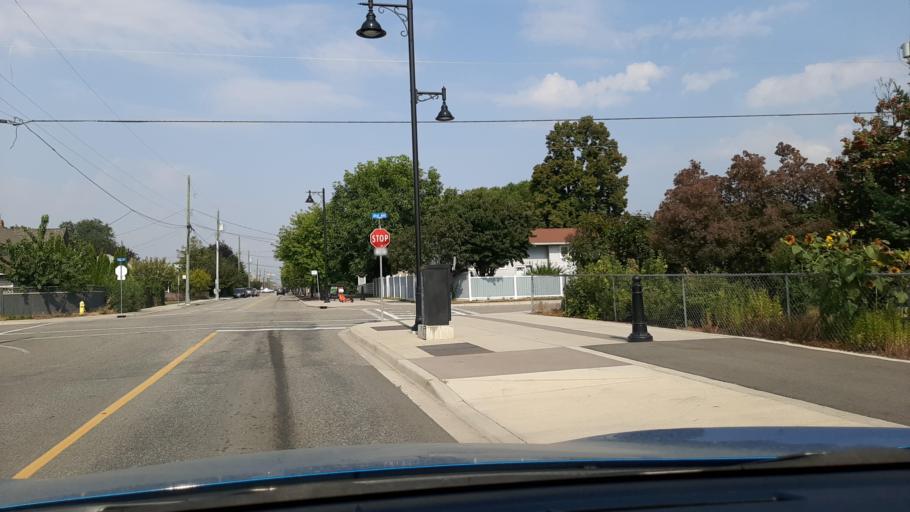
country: CA
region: British Columbia
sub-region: Regional District of North Okanagan
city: Vernon
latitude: 50.2713
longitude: -119.2712
